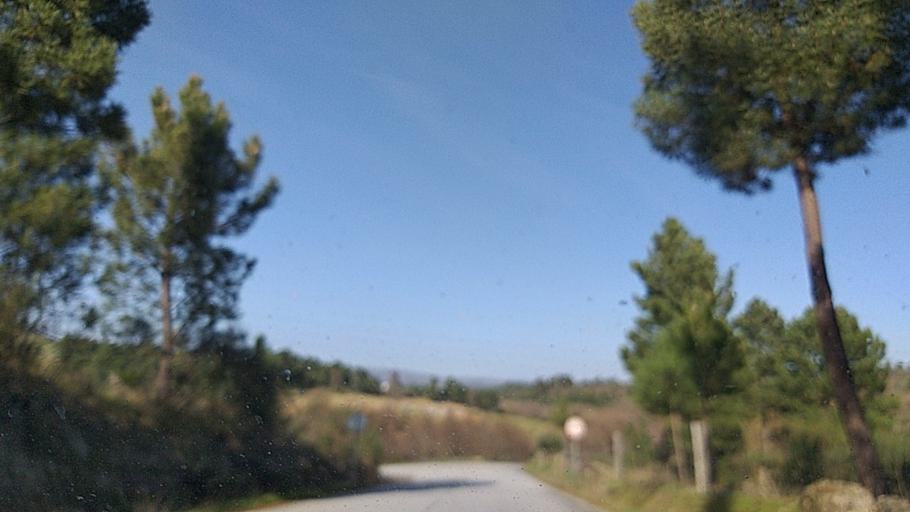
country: PT
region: Guarda
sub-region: Celorico da Beira
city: Celorico da Beira
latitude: 40.6448
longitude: -7.3951
